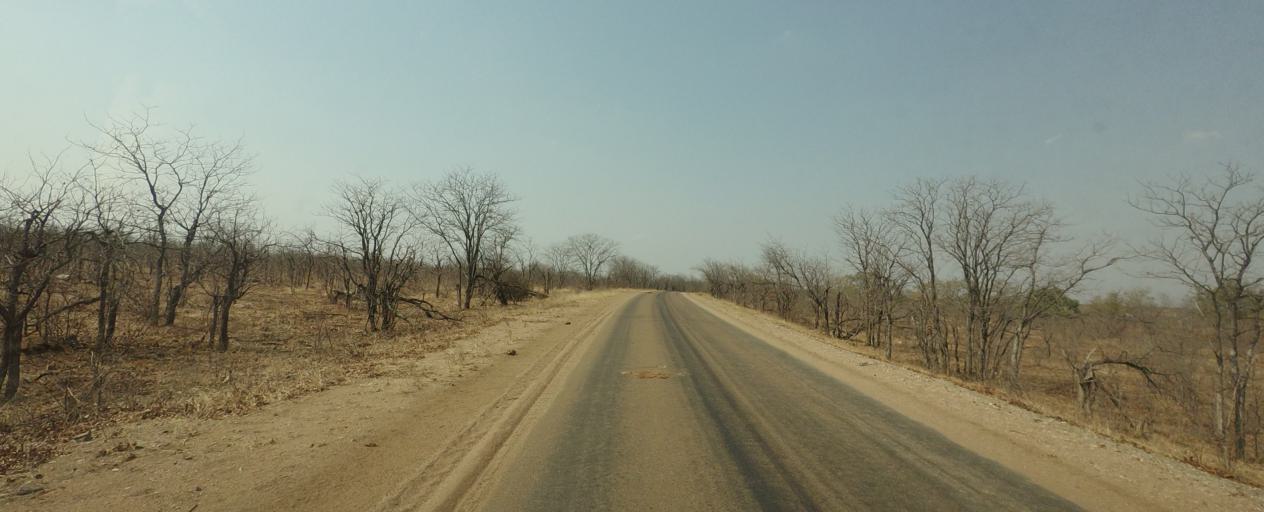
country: ZA
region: Limpopo
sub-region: Mopani District Municipality
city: Giyani
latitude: -23.1988
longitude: 31.3084
